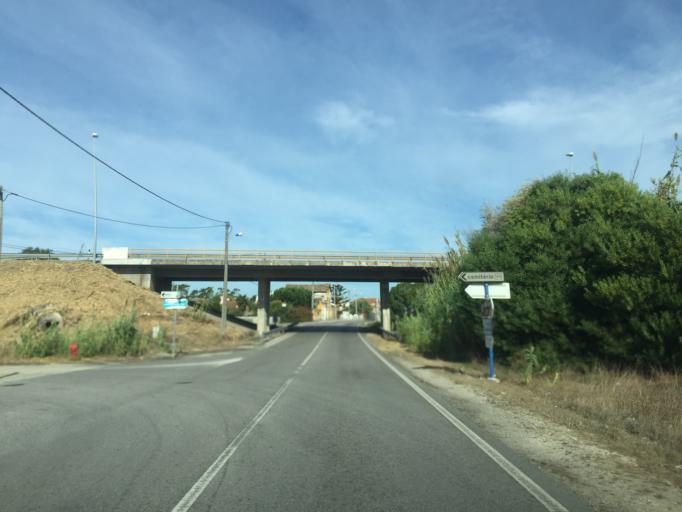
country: PT
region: Coimbra
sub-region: Figueira da Foz
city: Figueira da Foz
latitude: 40.1230
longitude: -8.8502
